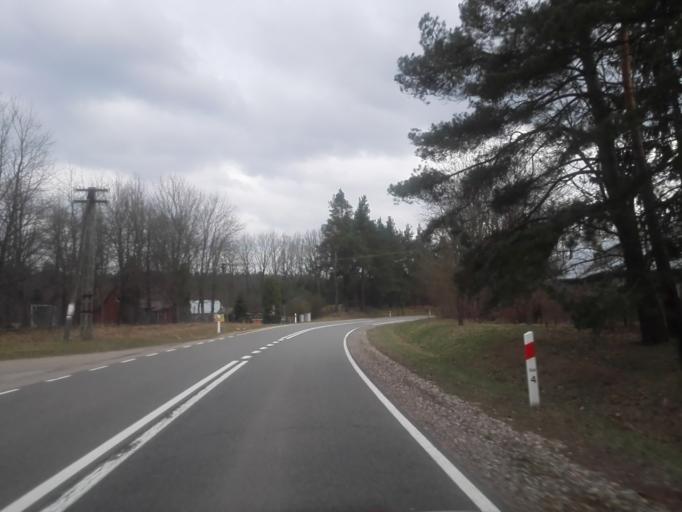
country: PL
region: Podlasie
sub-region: Powiat sejnenski
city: Sejny
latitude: 53.9810
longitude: 23.2935
